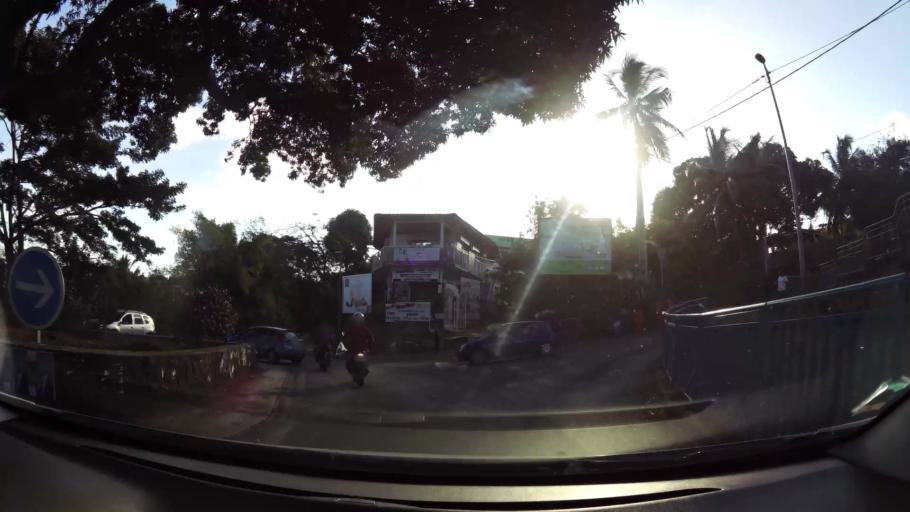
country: YT
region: Mamoudzou
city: Mamoudzou
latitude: -12.7851
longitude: 45.2279
